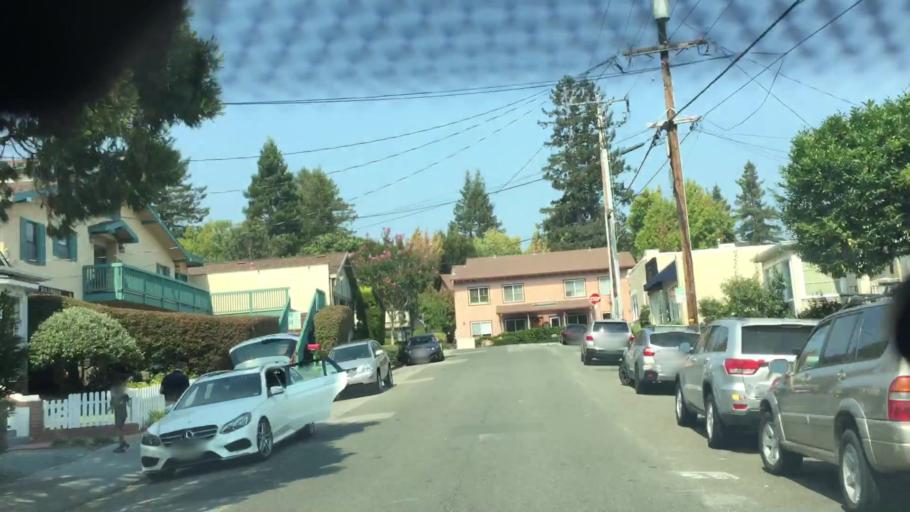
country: US
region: California
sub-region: Marin County
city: Mill Valley
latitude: 37.9040
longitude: -122.5432
